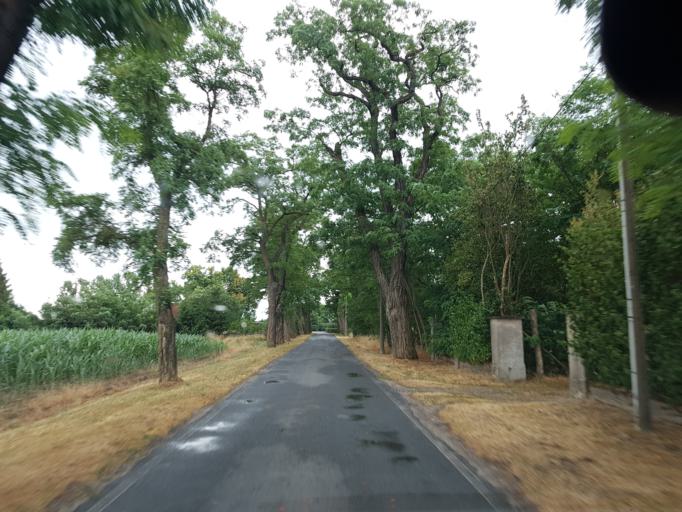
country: DE
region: Saxony-Anhalt
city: Seyda
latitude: 51.9244
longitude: 12.9173
